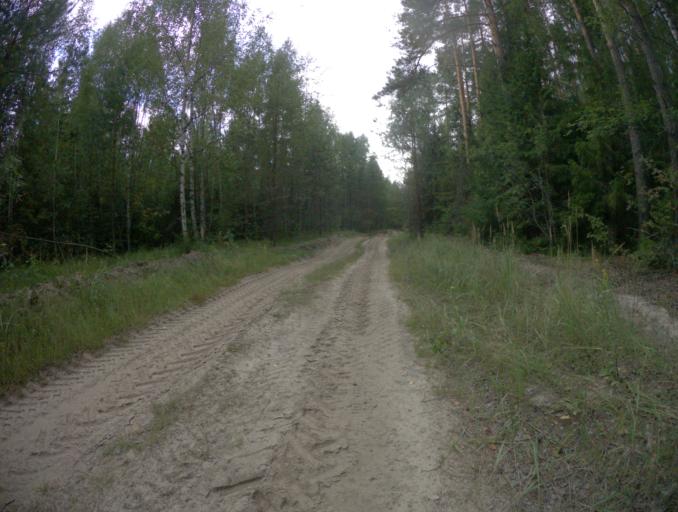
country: RU
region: Vladimir
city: Vorsha
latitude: 55.9572
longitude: 40.1501
